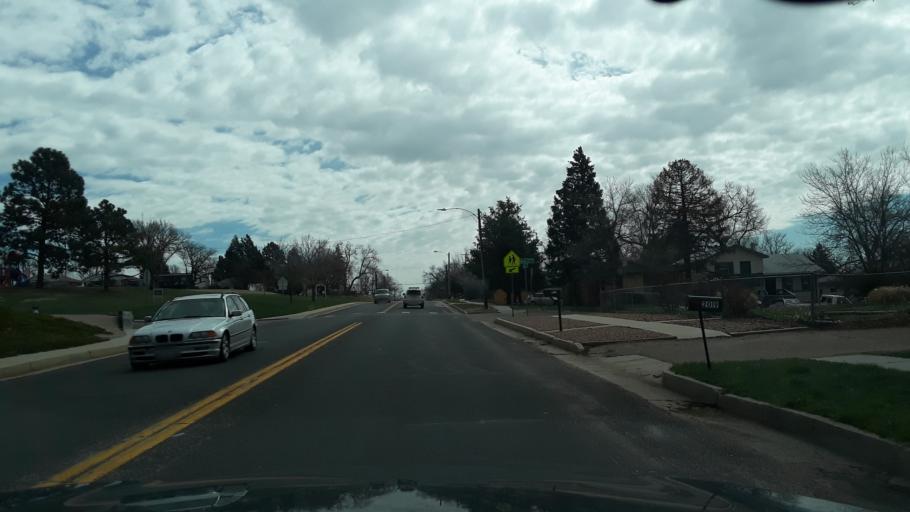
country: US
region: Colorado
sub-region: El Paso County
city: Colorado Springs
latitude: 38.8489
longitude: -104.7906
